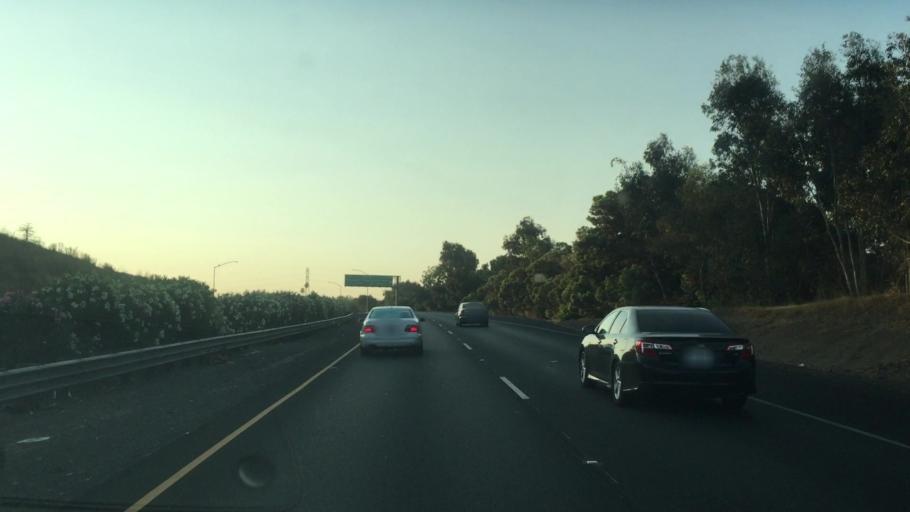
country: US
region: California
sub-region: Contra Costa County
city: Crockett
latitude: 38.0872
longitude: -122.2165
